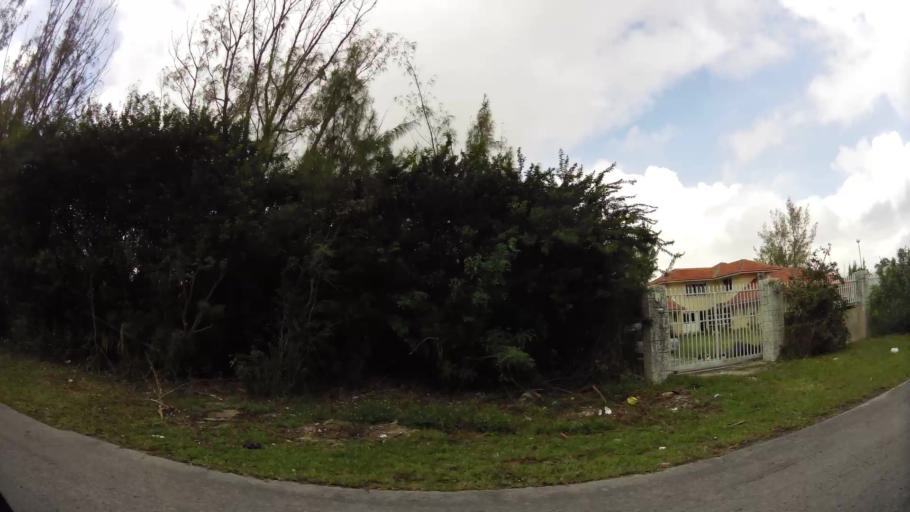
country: BS
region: Freeport
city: Lucaya
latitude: 26.5321
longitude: -78.6084
